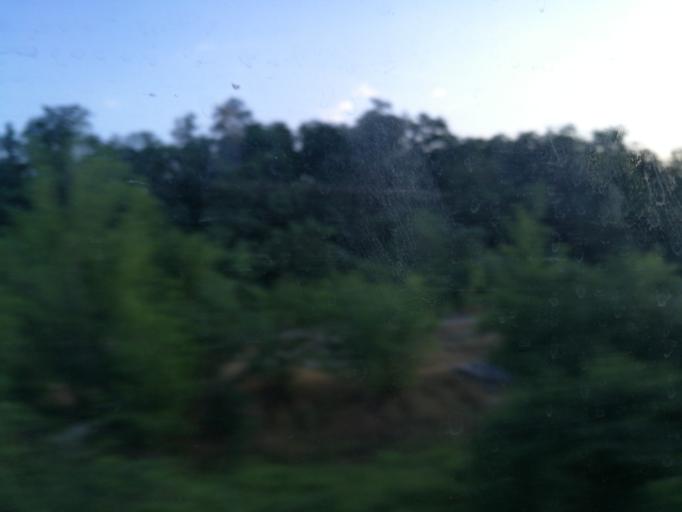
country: RO
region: Ilfov
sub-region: Comuna Buftea
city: Buciumeni
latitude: 44.5207
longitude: 25.9526
